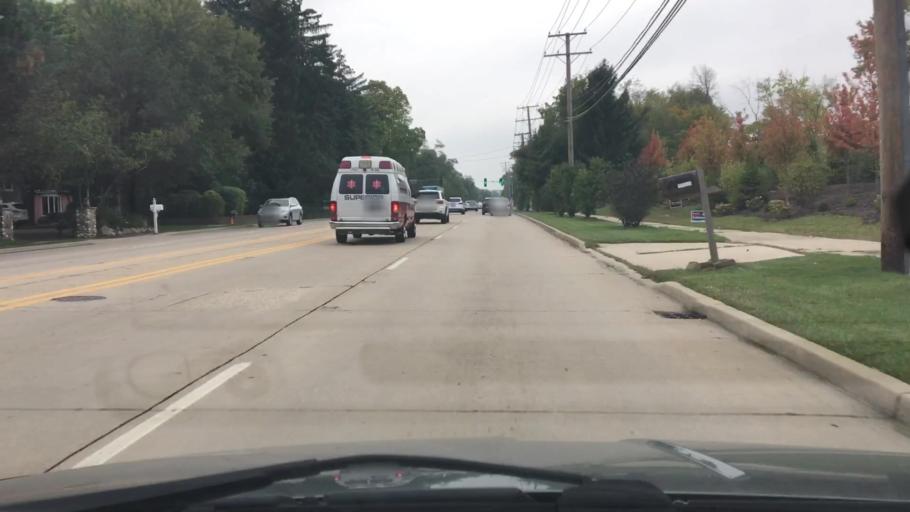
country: US
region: Illinois
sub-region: Lake County
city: Lincolnshire
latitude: 42.2005
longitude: -87.9136
